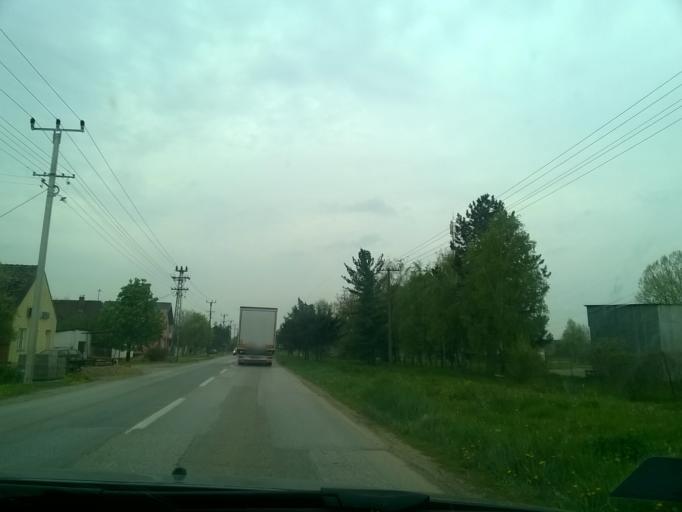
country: RS
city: Hrtkovci
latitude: 44.8854
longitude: 19.7635
